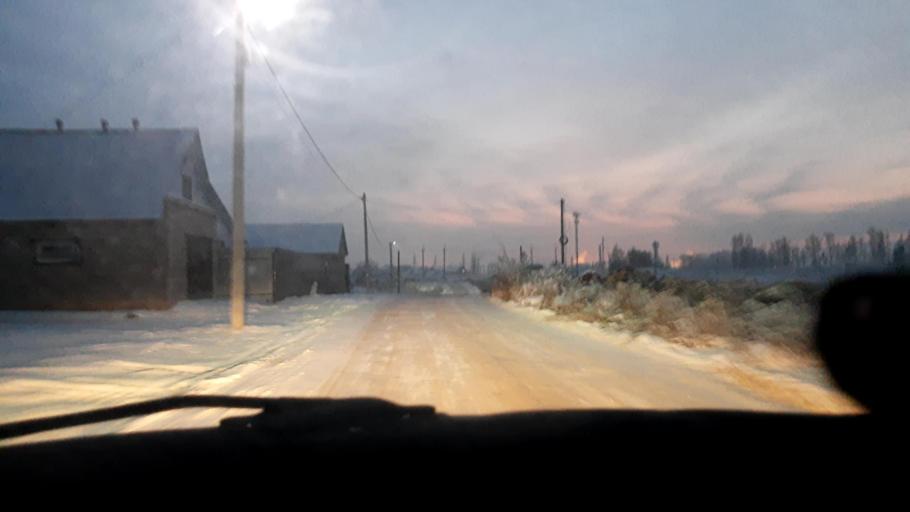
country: RU
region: Bashkortostan
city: Ufa
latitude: 54.8486
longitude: 56.0054
